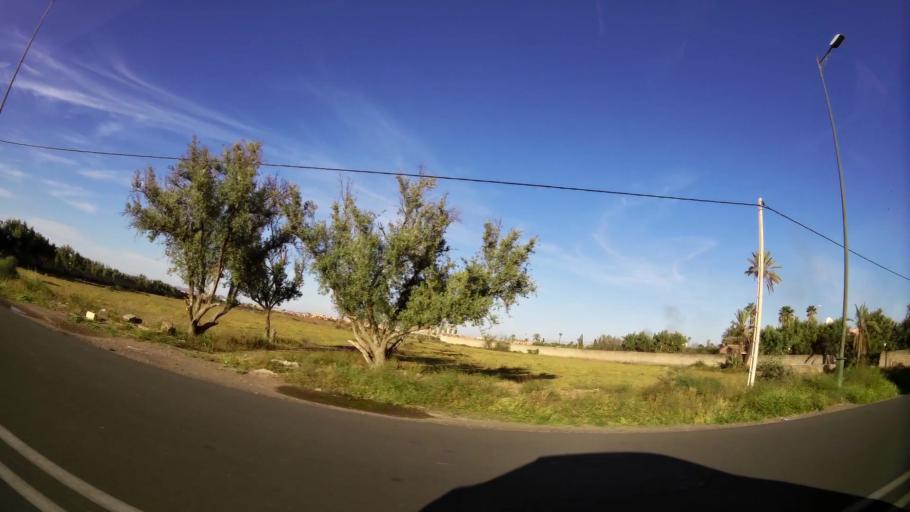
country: MA
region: Marrakech-Tensift-Al Haouz
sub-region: Marrakech
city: Marrakesh
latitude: 31.6645
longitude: -8.0562
